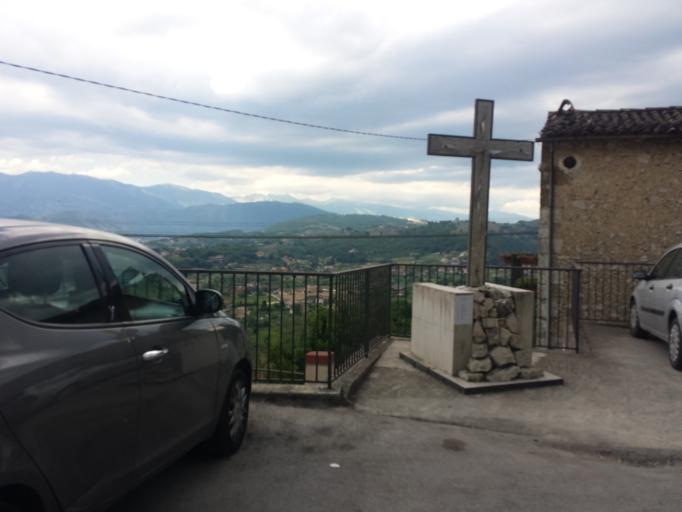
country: IT
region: Latium
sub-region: Provincia di Frosinone
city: Isola del Liri
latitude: 41.6789
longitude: 13.5906
